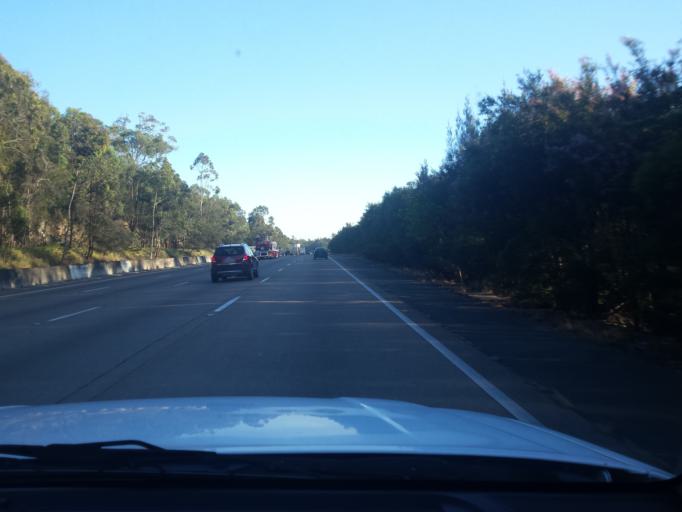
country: AU
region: Queensland
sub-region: Gold Coast
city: Oxenford
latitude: -27.8404
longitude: 153.3036
